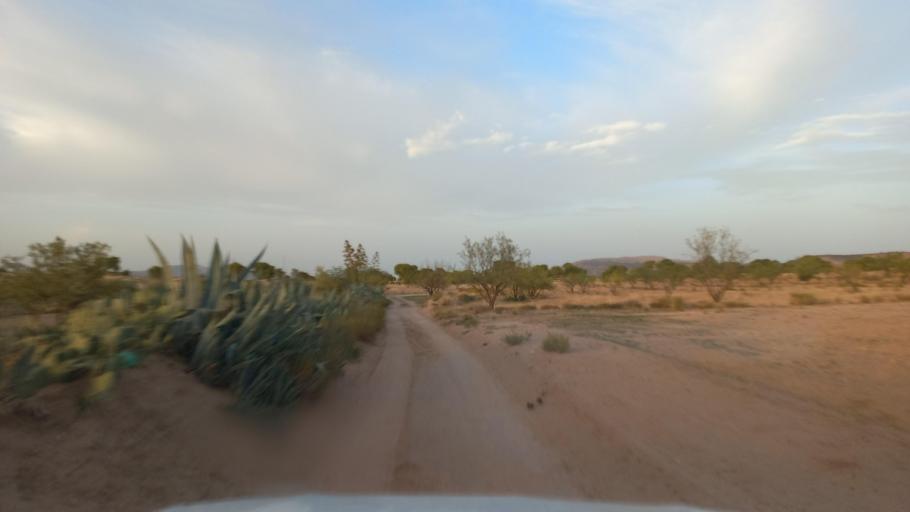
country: TN
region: Al Qasrayn
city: Sbiba
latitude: 35.4229
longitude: 8.9113
